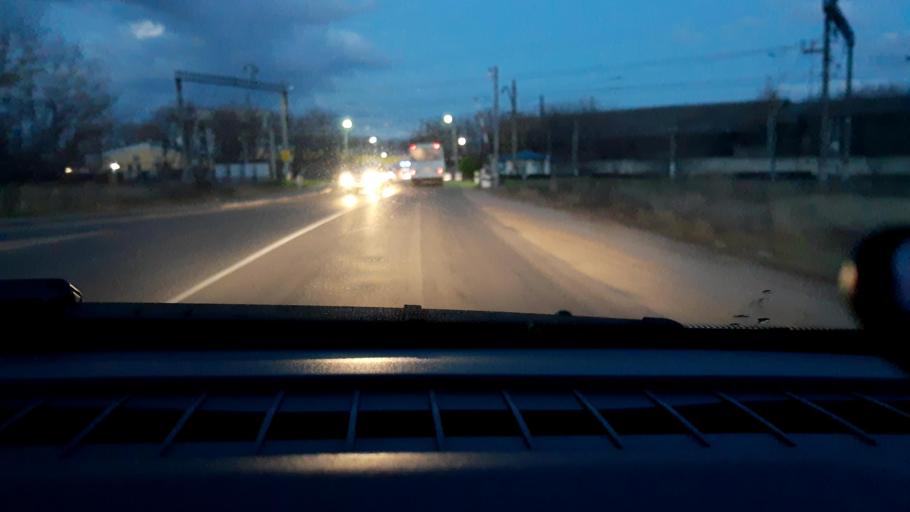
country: RU
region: Nizjnij Novgorod
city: Novaya Balakhna
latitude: 56.4858
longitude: 43.5762
